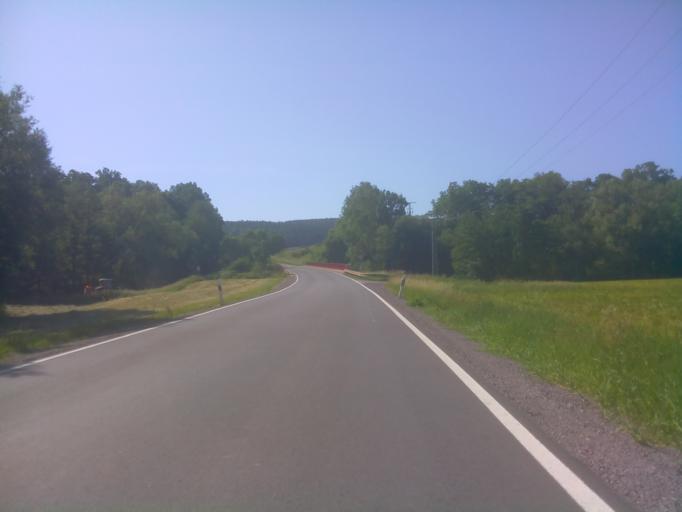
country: DE
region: Thuringia
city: Rudolstadt
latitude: 50.7197
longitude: 11.3980
